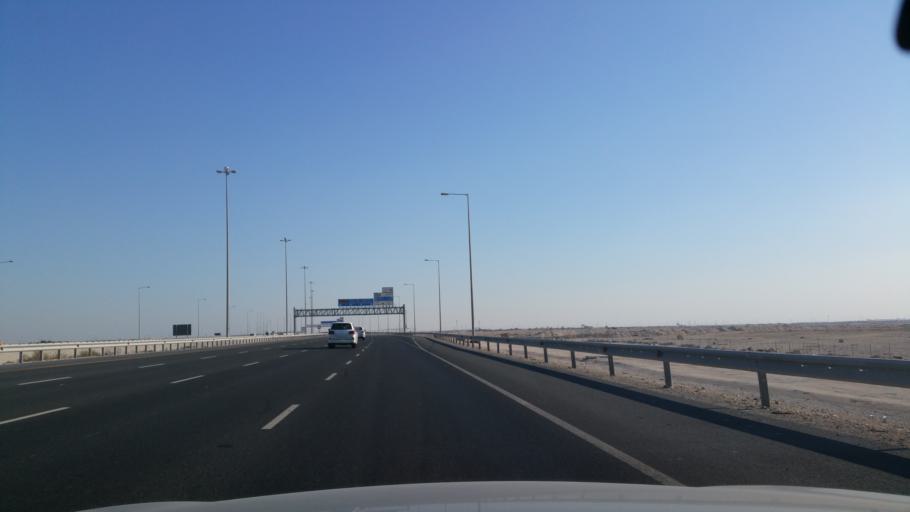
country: QA
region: Al Wakrah
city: Al Wukayr
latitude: 25.1416
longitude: 51.4756
